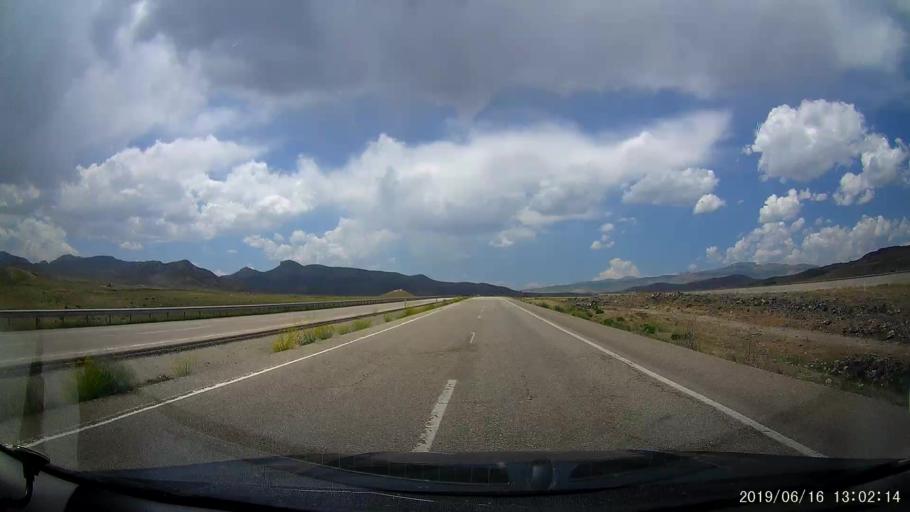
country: TR
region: Agri
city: Sulucem
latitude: 39.5733
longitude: 43.8216
